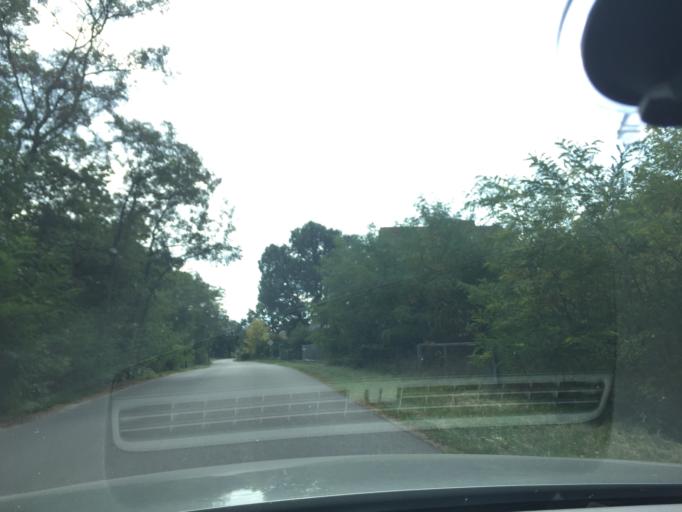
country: DE
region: Brandenburg
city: Grunheide
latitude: 52.3767
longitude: 13.7978
